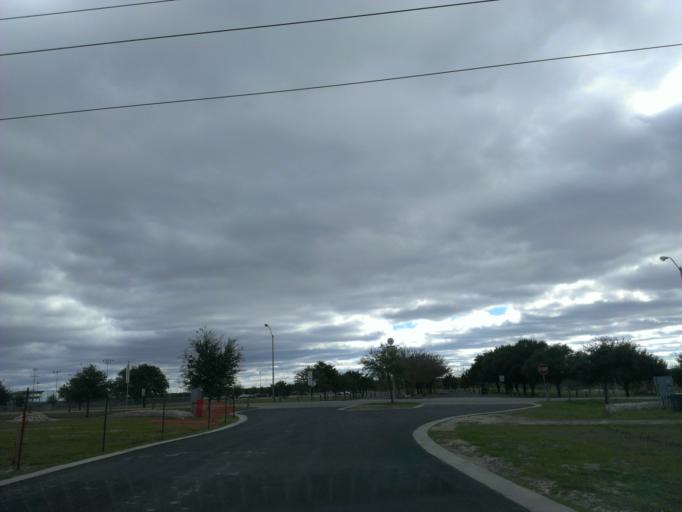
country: US
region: Texas
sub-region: Williamson County
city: Round Rock
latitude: 30.5444
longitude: -97.6260
